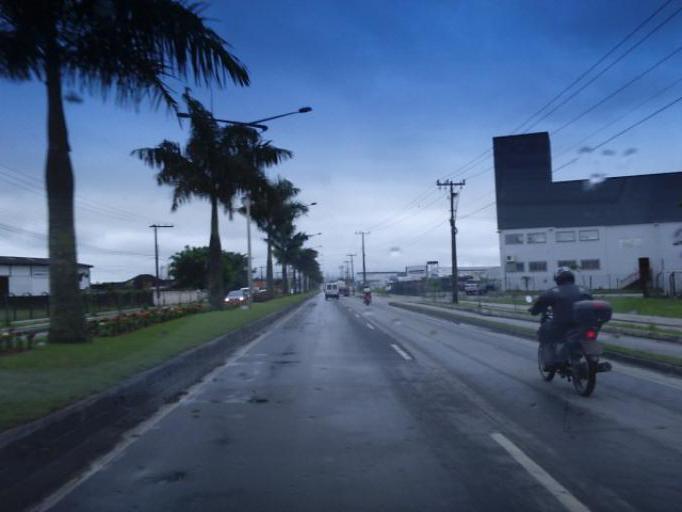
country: BR
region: Santa Catarina
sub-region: Itajai
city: Itajai
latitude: -26.9164
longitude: -48.7031
